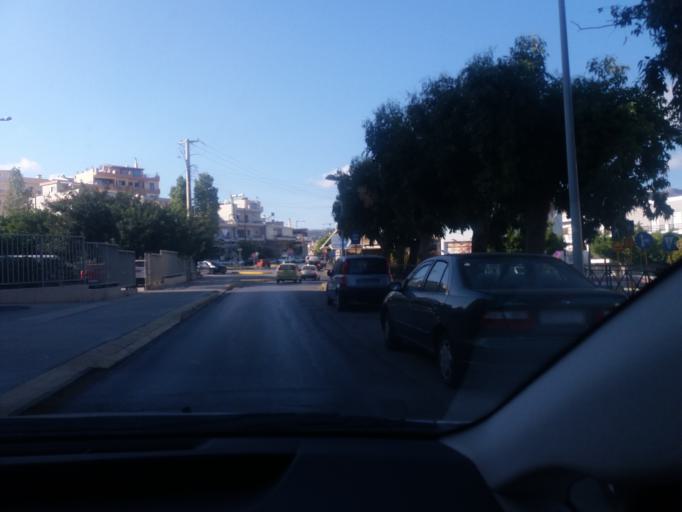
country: GR
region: Crete
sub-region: Nomos Lasithiou
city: Agios Nikolaos
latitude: 35.1946
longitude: 25.7138
